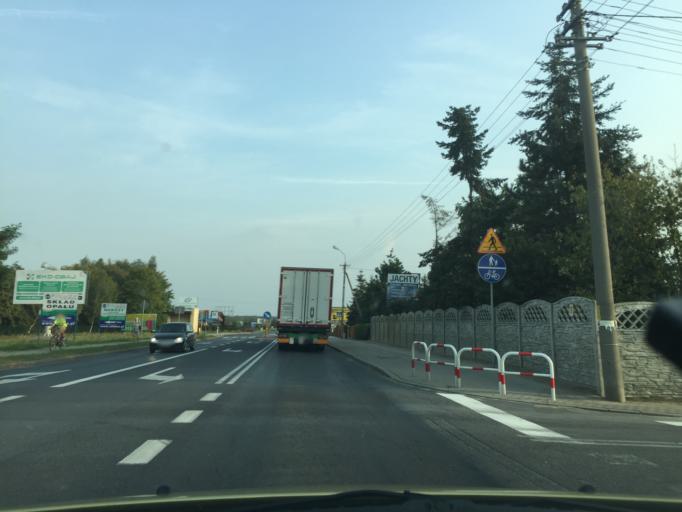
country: PL
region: Greater Poland Voivodeship
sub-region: Powiat jarocinski
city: Jarocin
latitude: 52.0062
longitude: 17.4740
